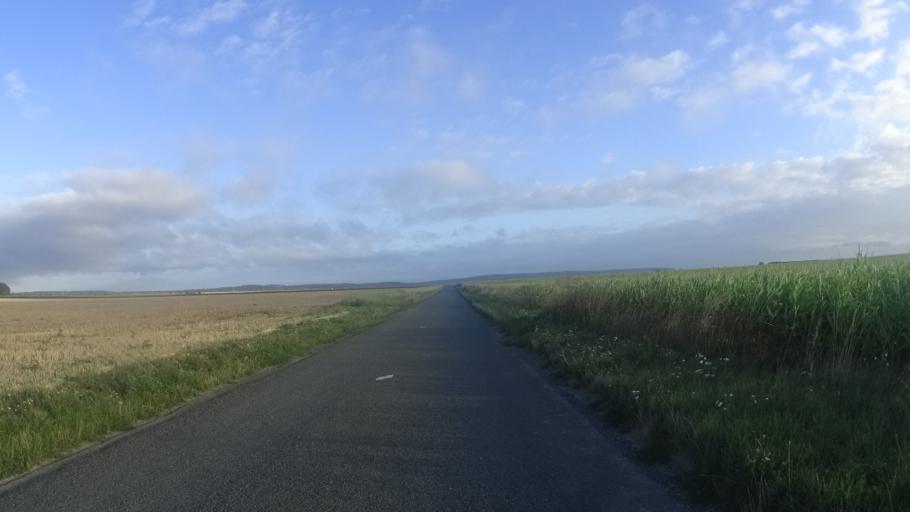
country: FR
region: Picardie
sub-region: Departement de l'Oise
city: Chamant
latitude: 49.2015
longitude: 2.6674
